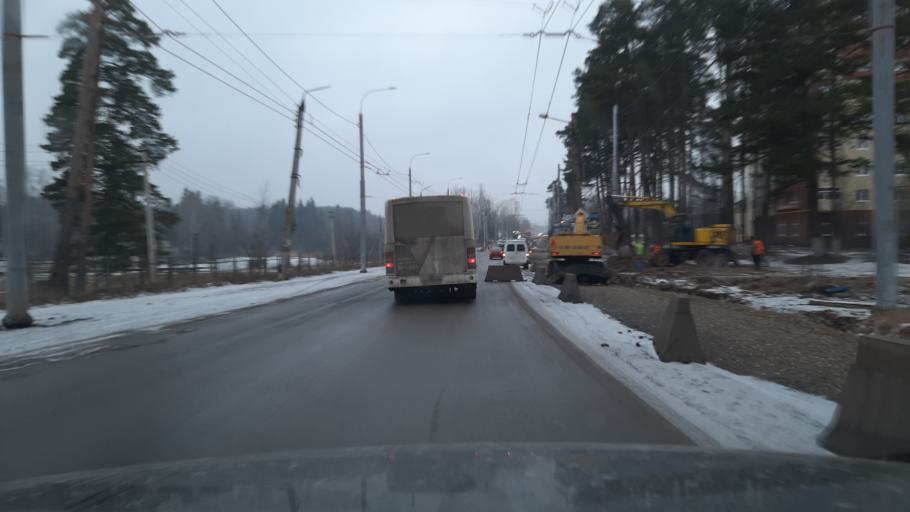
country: RU
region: Ivanovo
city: Kokhma
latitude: 56.9355
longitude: 41.0709
